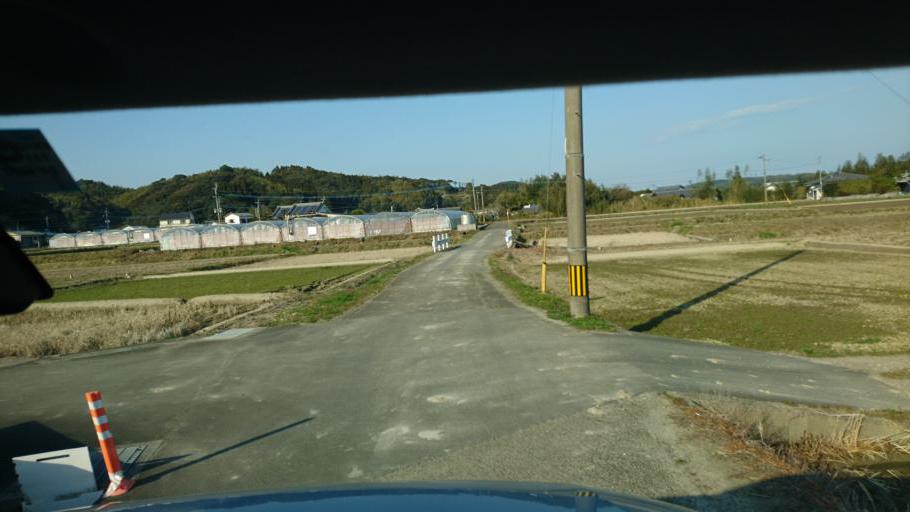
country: JP
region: Miyazaki
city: Miyazaki-shi
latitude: 32.0063
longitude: 131.4369
